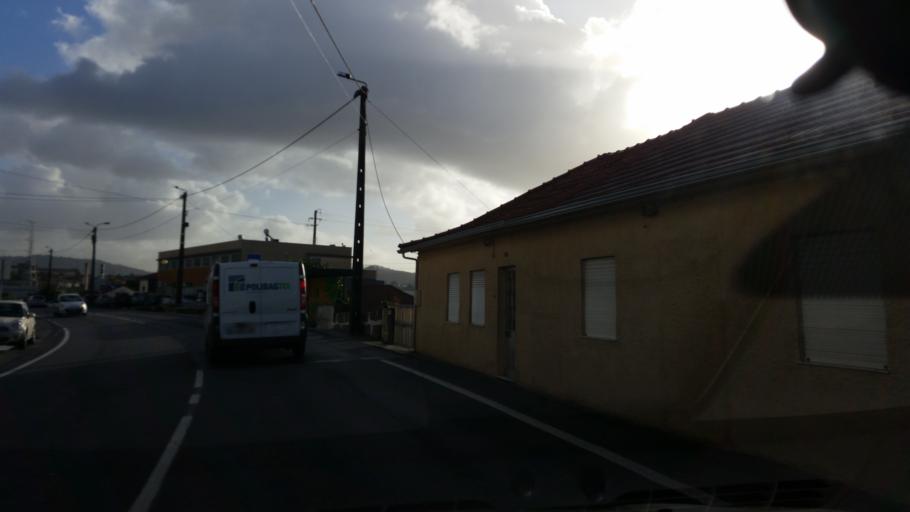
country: PT
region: Braga
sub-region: Guimaraes
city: Lordelo
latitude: 41.3689
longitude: -8.3833
